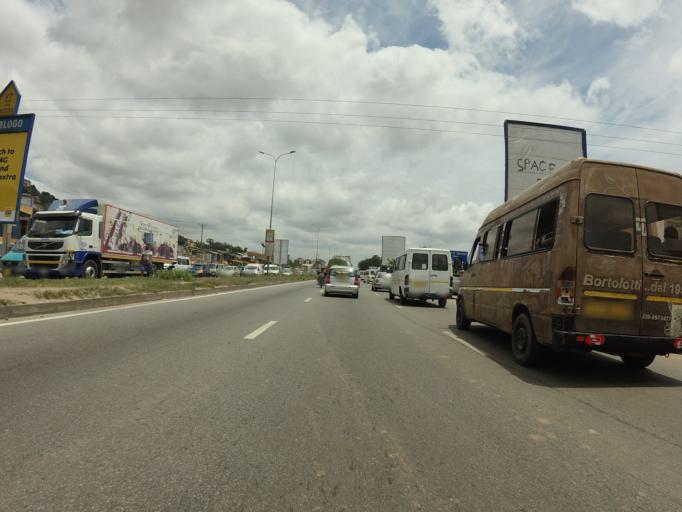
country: GH
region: Greater Accra
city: Gbawe
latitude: 5.5561
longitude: -0.3026
